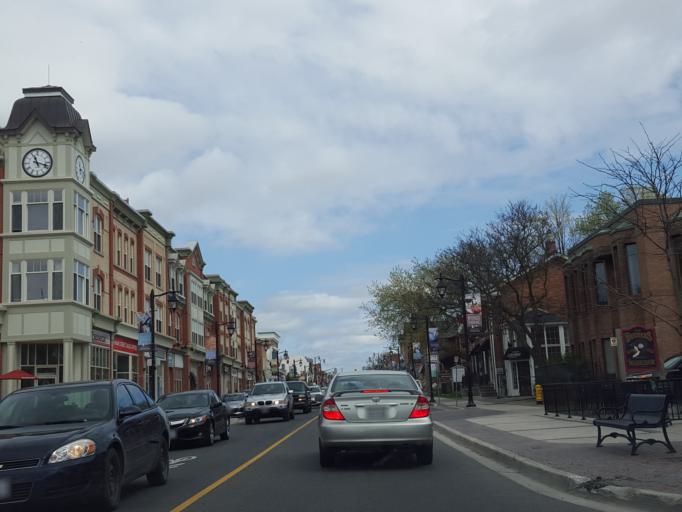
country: CA
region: Ontario
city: Markham
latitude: 43.8759
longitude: -79.2603
